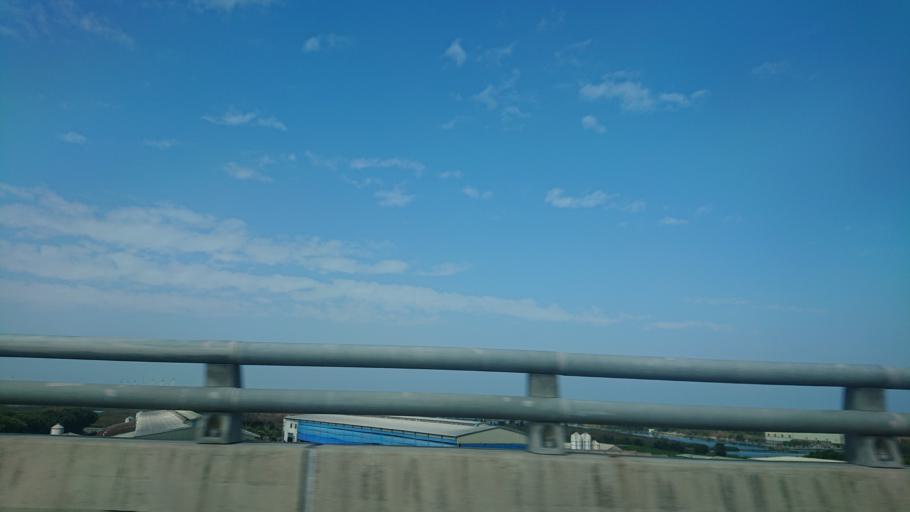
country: TW
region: Taiwan
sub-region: Changhua
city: Chang-hua
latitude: 23.9854
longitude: 120.3674
